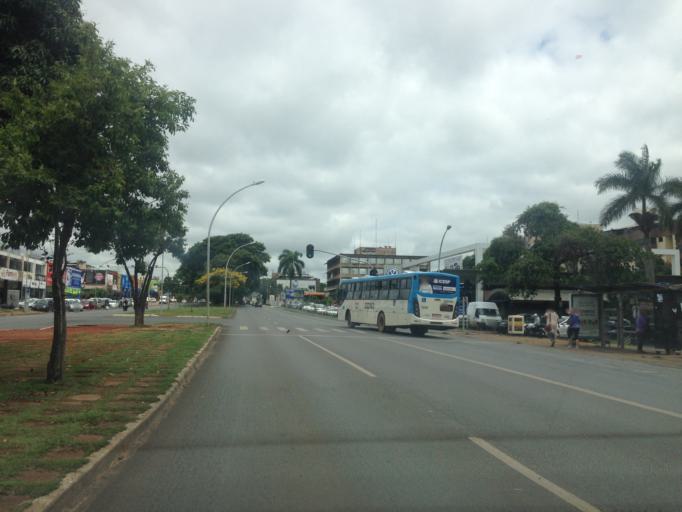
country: BR
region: Federal District
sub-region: Brasilia
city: Brasilia
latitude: -15.7811
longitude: -47.8876
